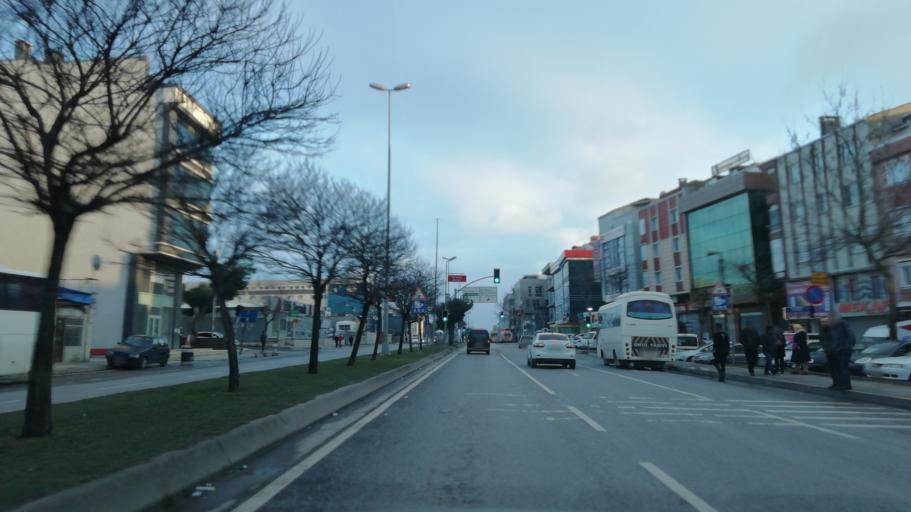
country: TR
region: Istanbul
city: Esenyurt
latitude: 41.0080
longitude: 28.7037
